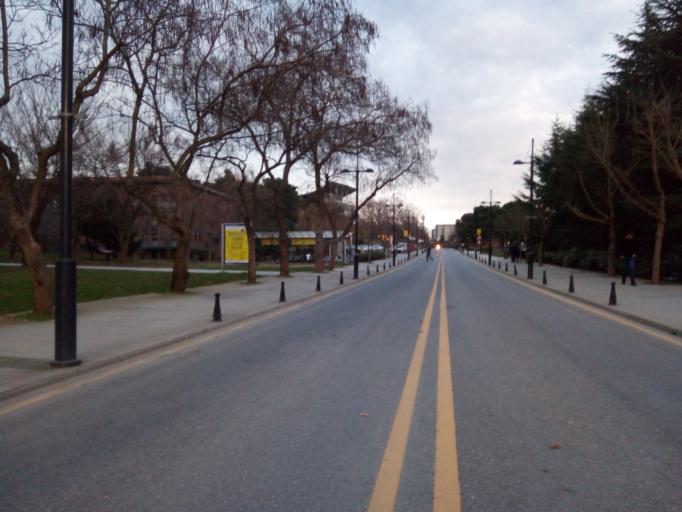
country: TR
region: Istanbul
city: Sisli
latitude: 41.1049
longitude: 29.0238
